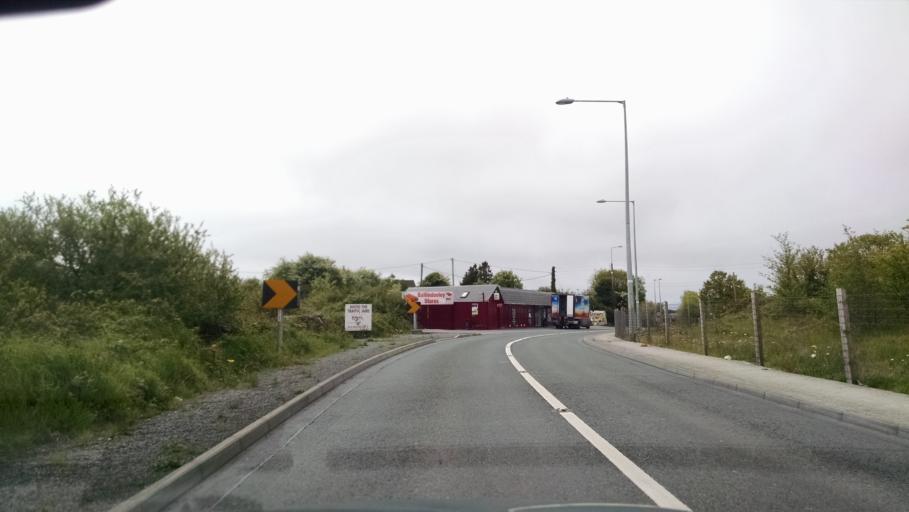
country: IE
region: Connaught
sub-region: County Galway
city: Gaillimh
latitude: 53.3146
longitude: -9.0225
